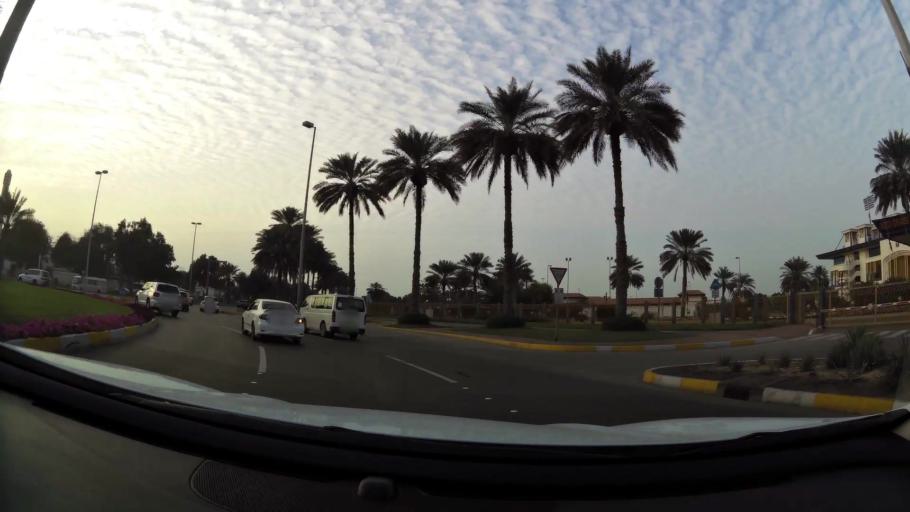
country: AE
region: Abu Dhabi
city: Abu Dhabi
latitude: 24.4423
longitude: 54.3749
